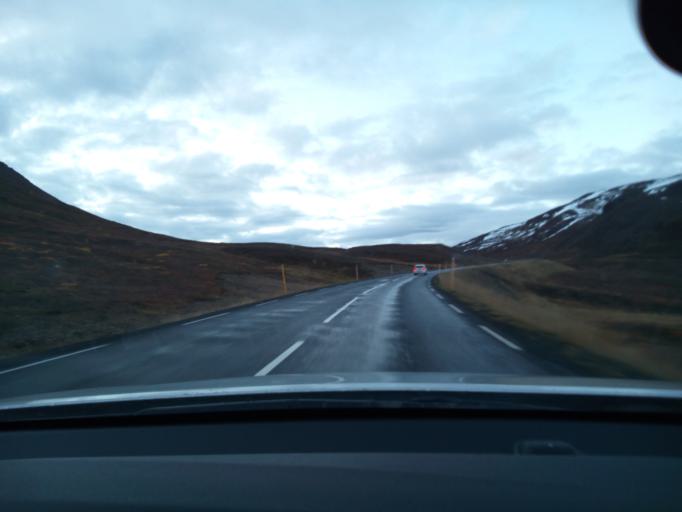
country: IS
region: Northeast
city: Akureyri
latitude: 65.7986
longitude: -17.9478
